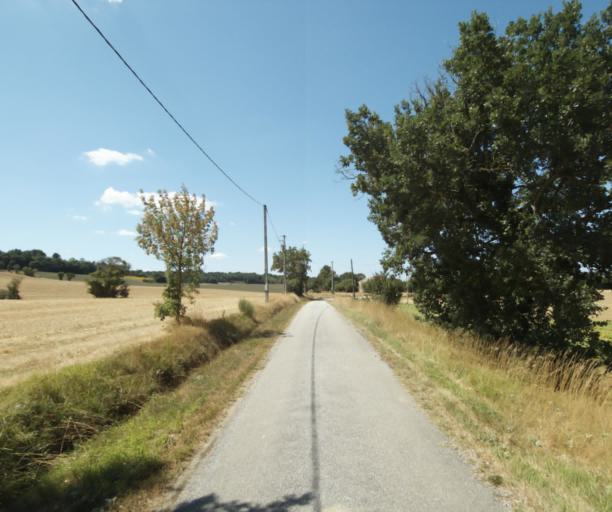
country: FR
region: Midi-Pyrenees
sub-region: Departement de la Haute-Garonne
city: Saint-Felix-Lauragais
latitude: 43.4743
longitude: 1.8807
